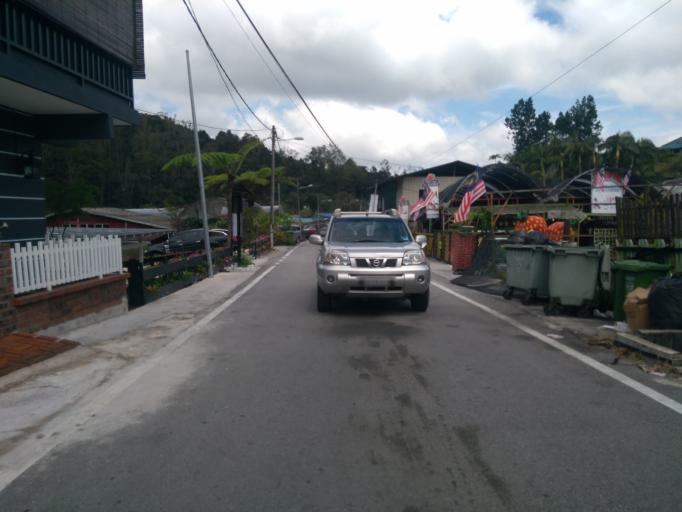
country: MY
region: Pahang
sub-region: Cameron Highlands
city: Tanah Rata
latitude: 4.4794
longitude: 101.3807
